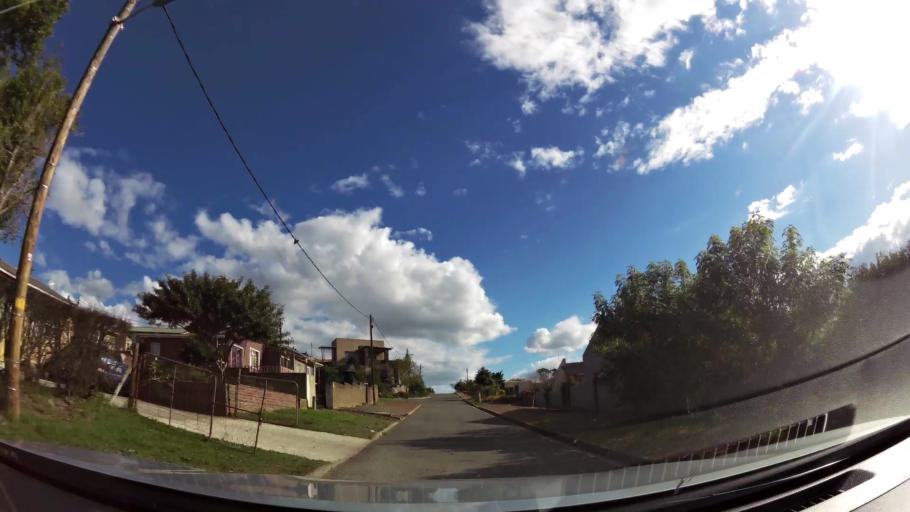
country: ZA
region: Western Cape
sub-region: Overberg District Municipality
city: Swellendam
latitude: -34.0323
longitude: 20.4413
